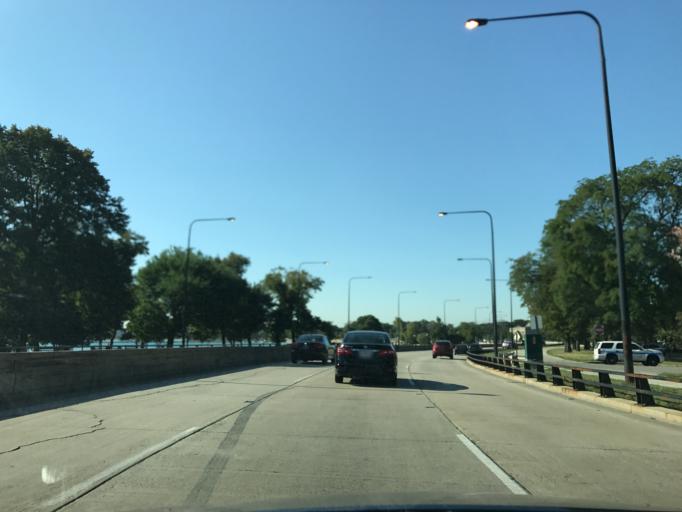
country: US
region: Illinois
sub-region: Cook County
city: Chicago
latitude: 41.7960
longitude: -87.5792
